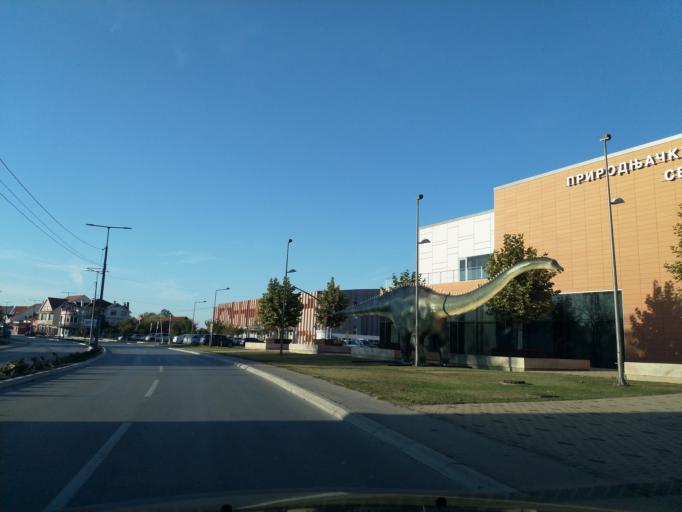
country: RS
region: Central Serbia
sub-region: Pomoravski Okrug
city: Svilajnac
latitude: 44.2313
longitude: 21.1922
